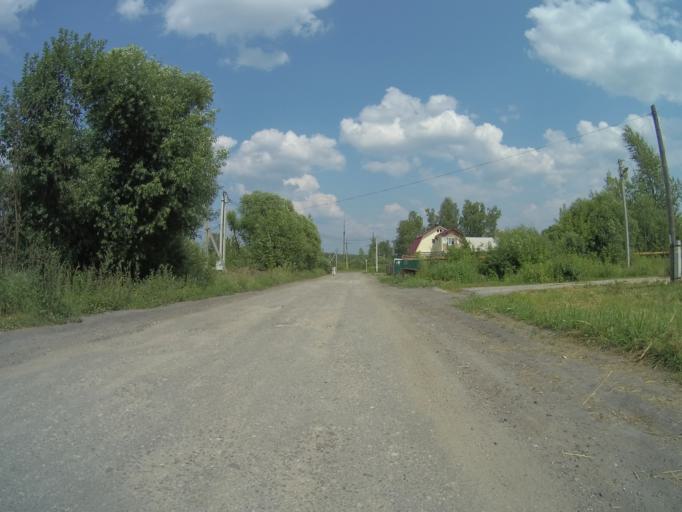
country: RU
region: Vladimir
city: Kommunar
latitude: 56.0456
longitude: 40.5360
